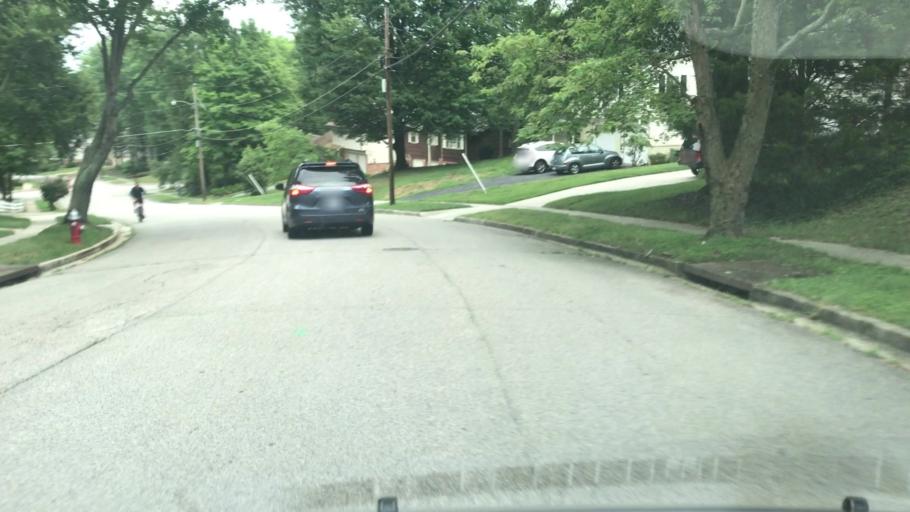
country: US
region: Virginia
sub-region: Fairfax County
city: Mount Vernon
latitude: 38.7236
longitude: -77.0884
